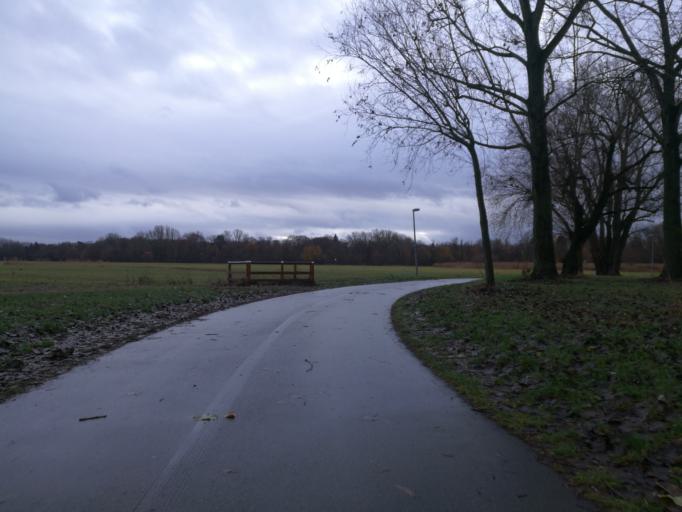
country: DE
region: Bavaria
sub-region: Regierungsbezirk Mittelfranken
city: Furth
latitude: 49.4787
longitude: 10.9942
